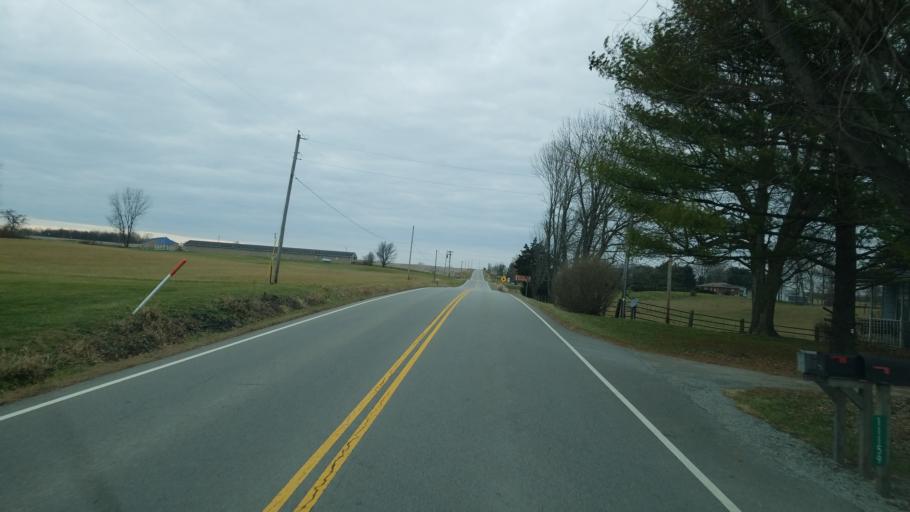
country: US
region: Ohio
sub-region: Highland County
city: Hillsboro
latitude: 39.2165
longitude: -83.4822
